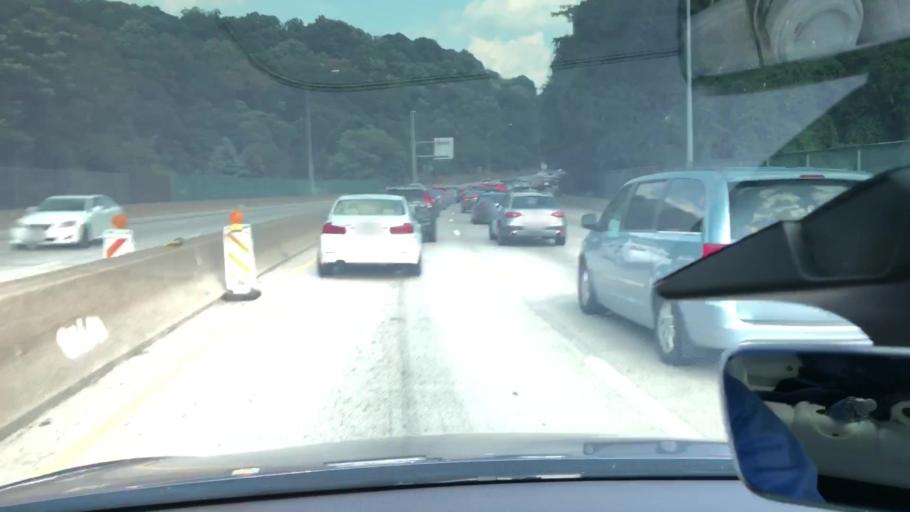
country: US
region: Pennsylvania
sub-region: Allegheny County
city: Bloomfield
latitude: 40.4288
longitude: -79.9436
